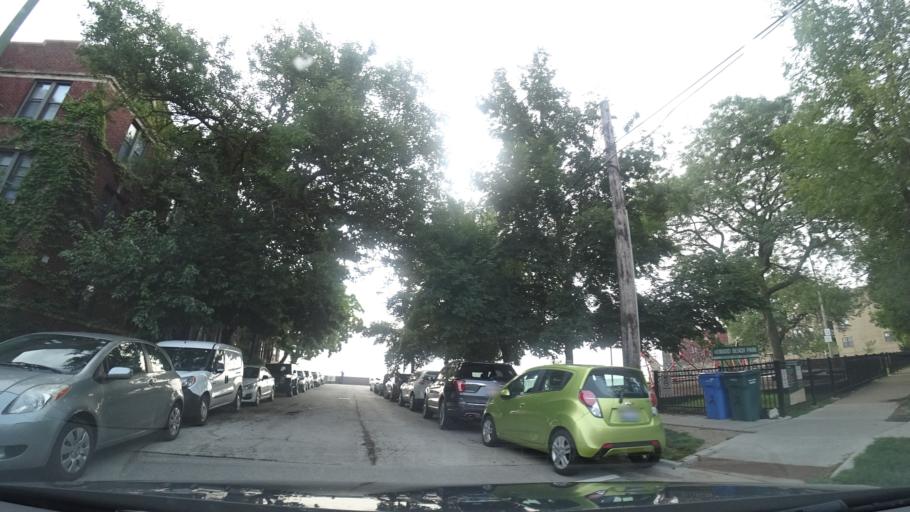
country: US
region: Illinois
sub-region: Cook County
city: Evanston
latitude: 42.0193
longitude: -87.6645
